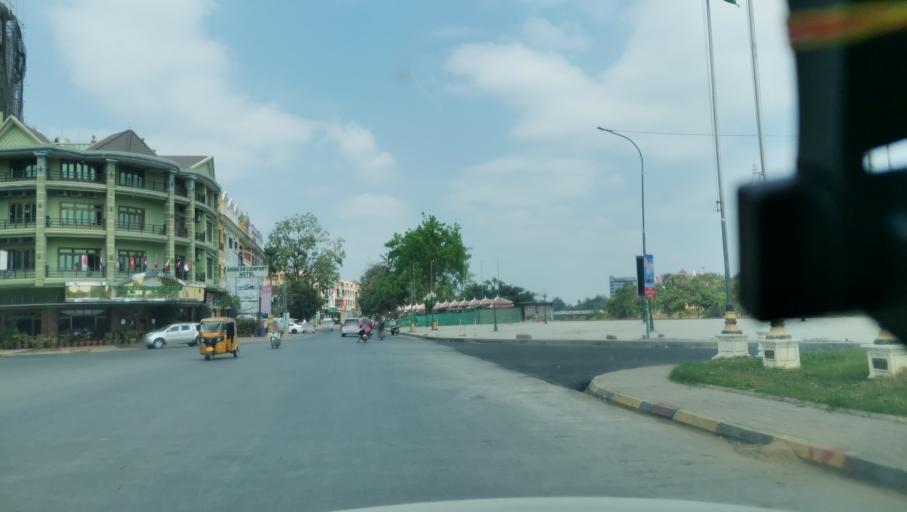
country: KH
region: Battambang
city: Battambang
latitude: 13.0937
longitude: 103.1985
